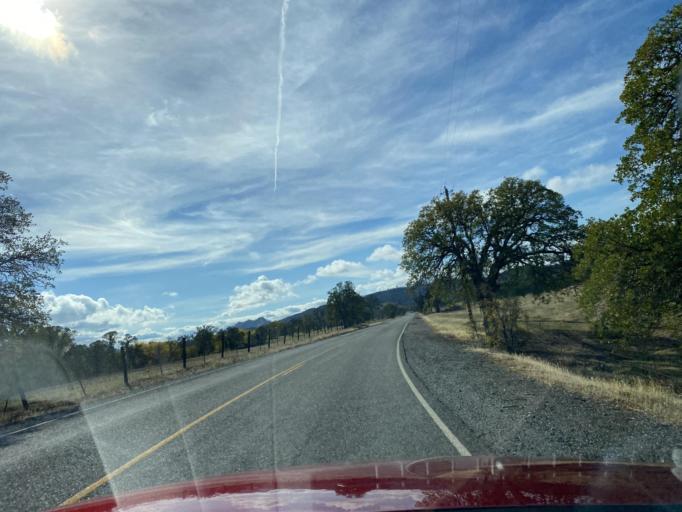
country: US
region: California
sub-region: Glenn County
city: Willows
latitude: 39.4626
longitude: -122.5112
